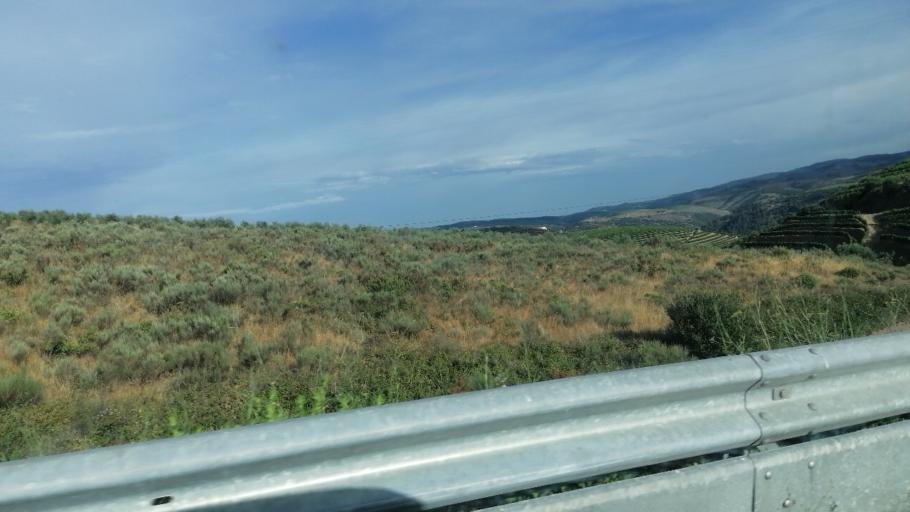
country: PT
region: Viseu
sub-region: Sao Joao da Pesqueira
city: Sao Joao da Pesqueira
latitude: 41.1333
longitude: -7.4390
